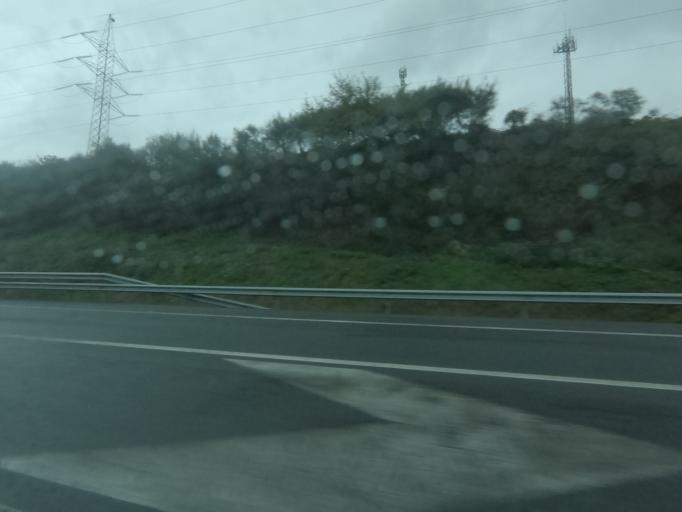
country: ES
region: Galicia
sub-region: Provincia de Pontevedra
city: Pontevedra
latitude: 42.3924
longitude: -8.6417
